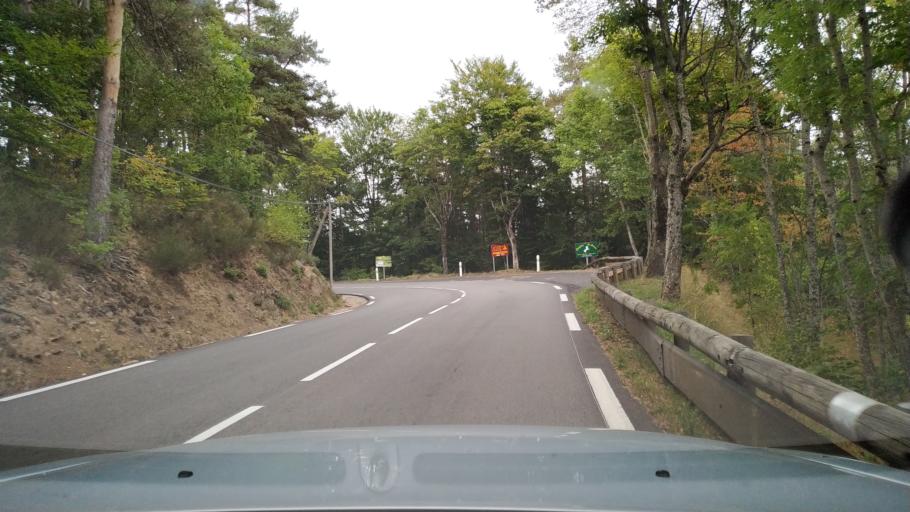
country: FR
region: Rhone-Alpes
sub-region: Departement de l'Ardeche
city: Saint-Agreve
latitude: 45.0031
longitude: 4.4091
